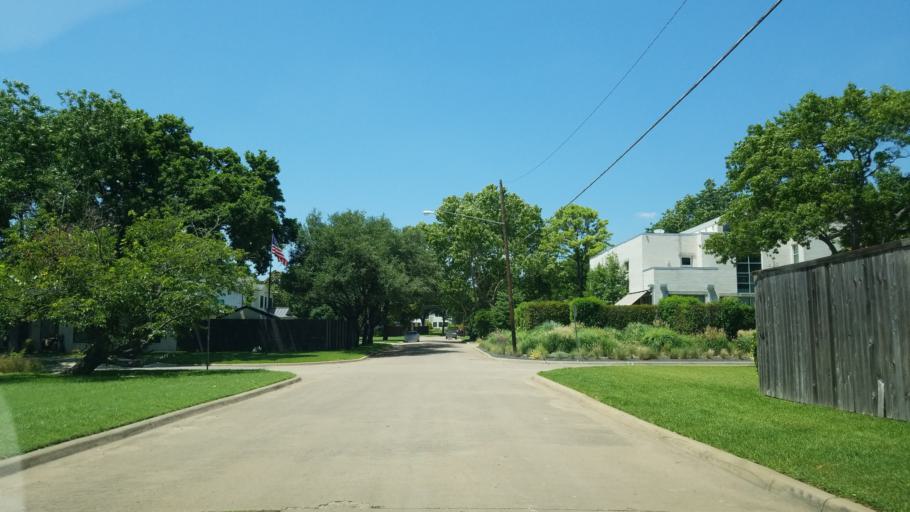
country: US
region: Texas
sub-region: Dallas County
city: University Park
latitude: 32.8715
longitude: -96.8450
